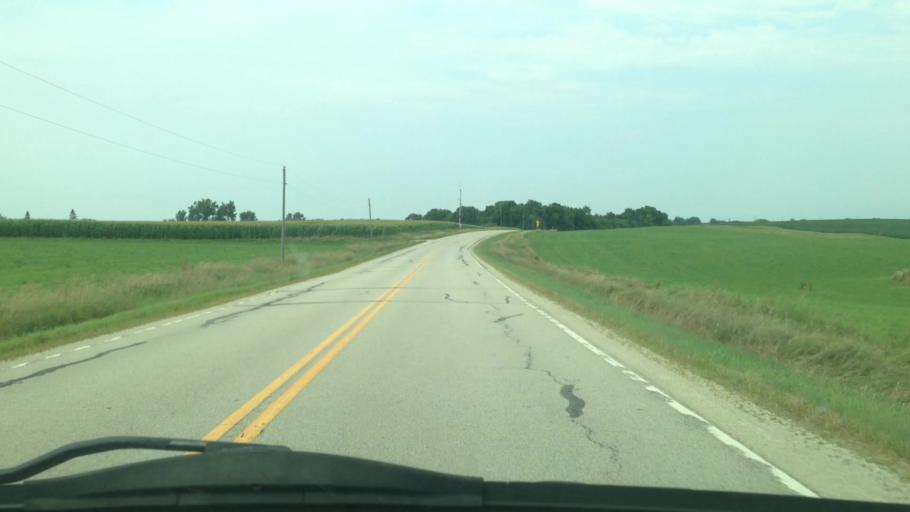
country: US
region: Minnesota
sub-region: Fillmore County
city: Preston
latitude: 43.7622
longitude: -91.9625
